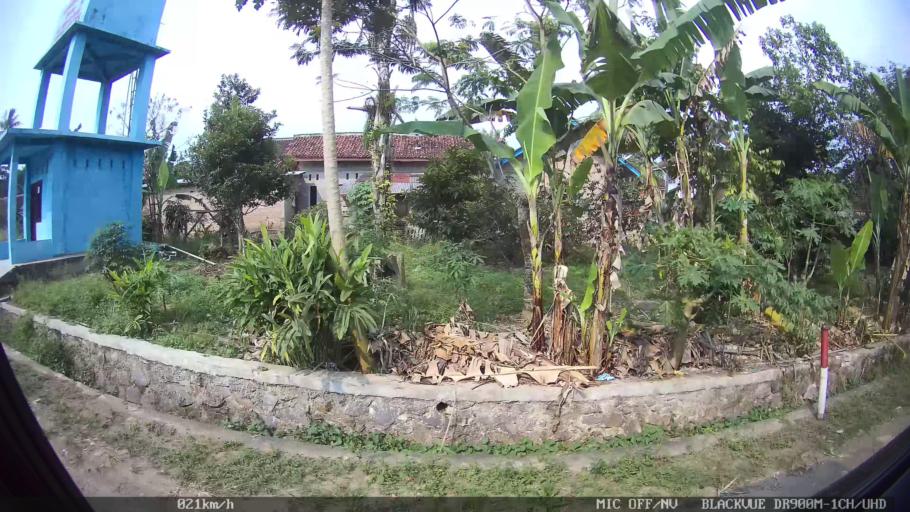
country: ID
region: Lampung
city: Gadingrejo
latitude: -5.4029
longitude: 105.0228
